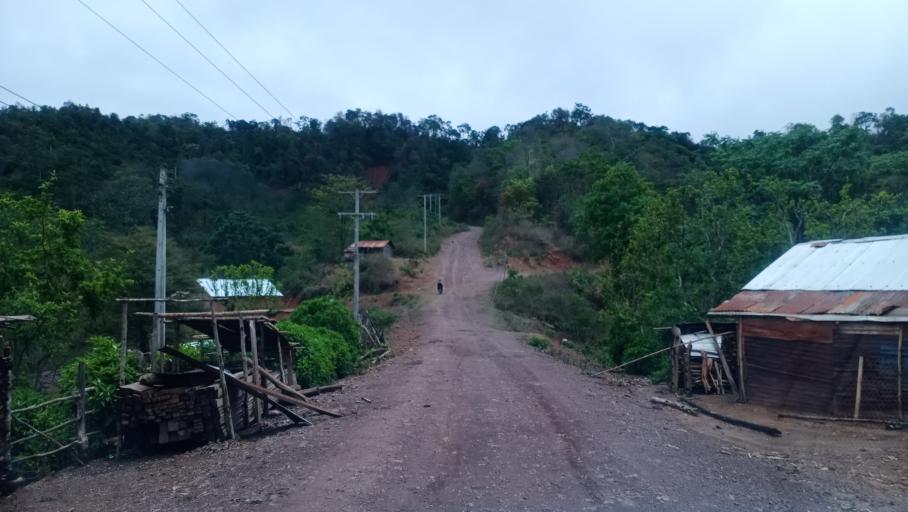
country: LA
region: Phongsali
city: Phongsali
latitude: 21.3460
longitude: 102.0938
